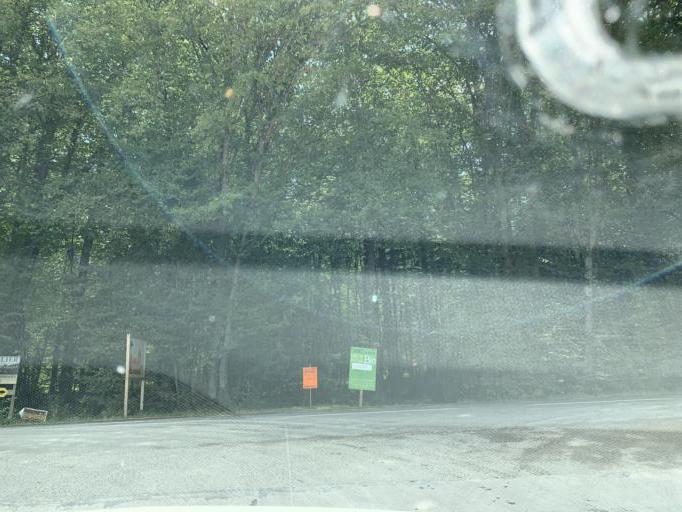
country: FR
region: Bourgogne
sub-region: Departement de la Nievre
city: Saint-Amand-en-Puisaye
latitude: 47.5812
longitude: 3.1556
